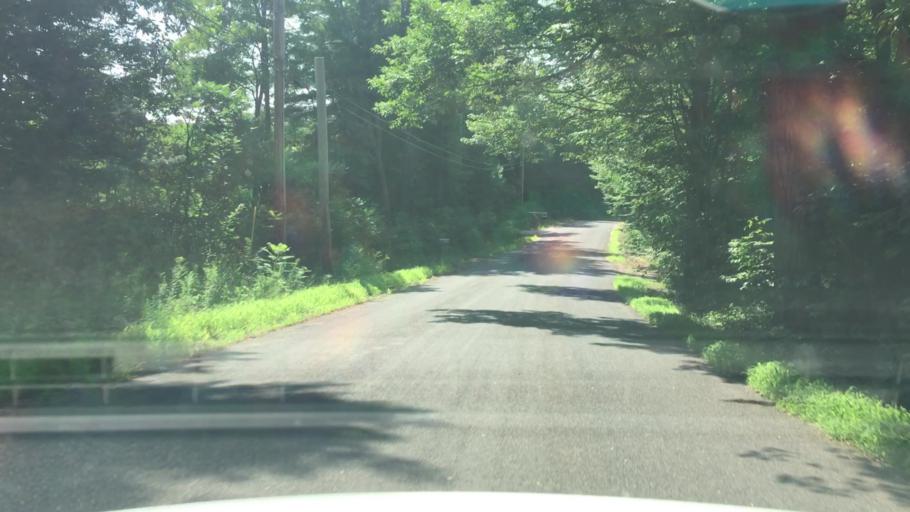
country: US
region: Maine
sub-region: Androscoggin County
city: Greene
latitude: 44.2233
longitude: -70.1046
